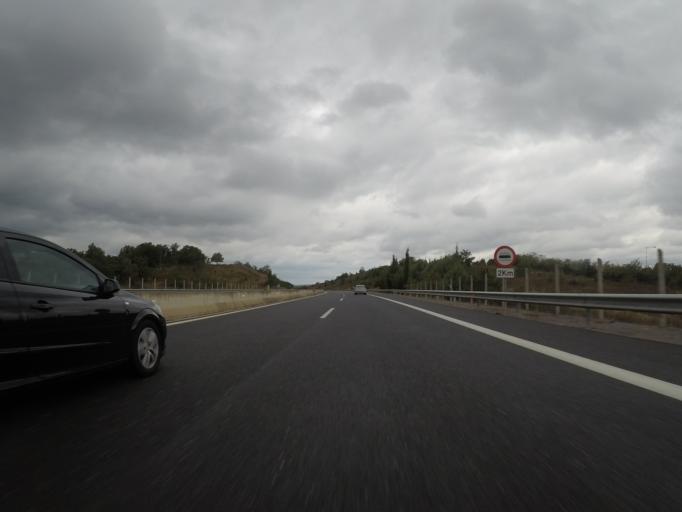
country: GR
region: Peloponnese
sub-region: Nomos Arkadias
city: Megalopoli
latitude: 37.3588
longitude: 22.1310
